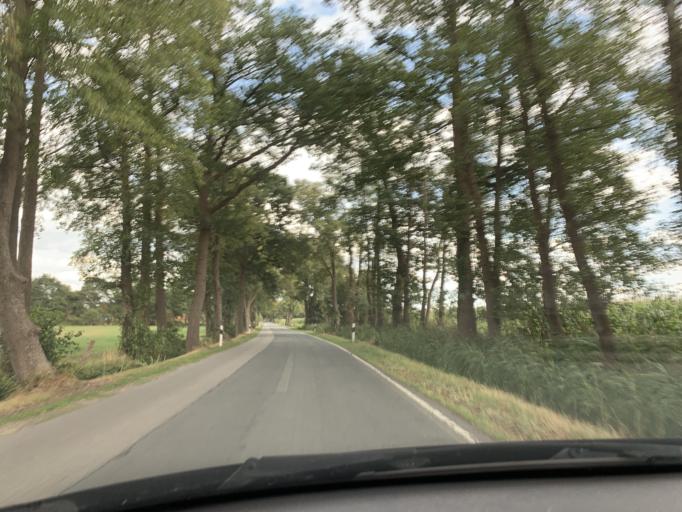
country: DE
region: Lower Saxony
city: Westerstede
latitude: 53.2201
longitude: 7.8757
